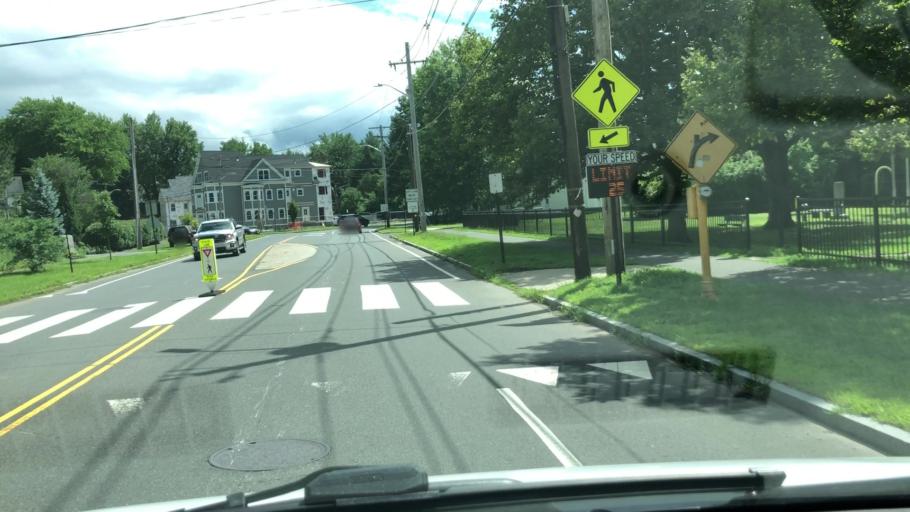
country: US
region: Massachusetts
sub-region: Hampshire County
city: Northampton
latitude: 42.3240
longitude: -72.6252
